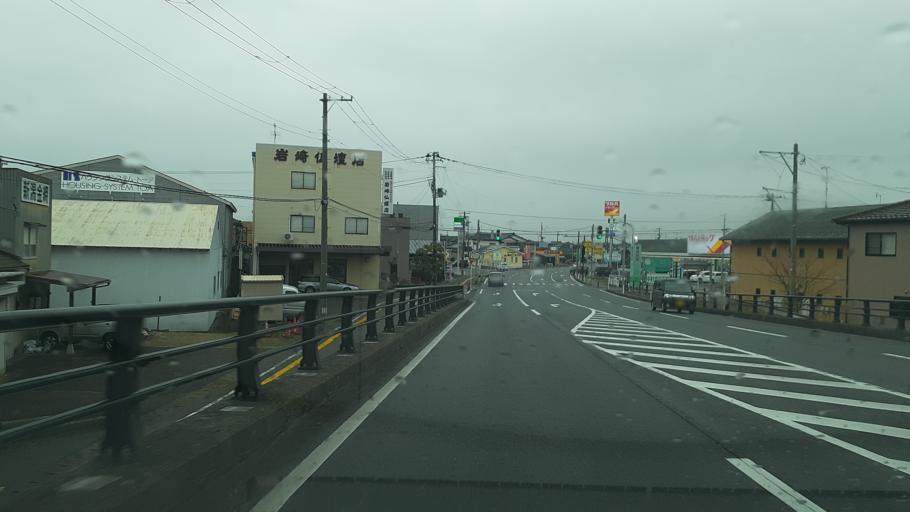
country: JP
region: Niigata
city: Kameda-honcho
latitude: 37.8754
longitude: 139.1108
